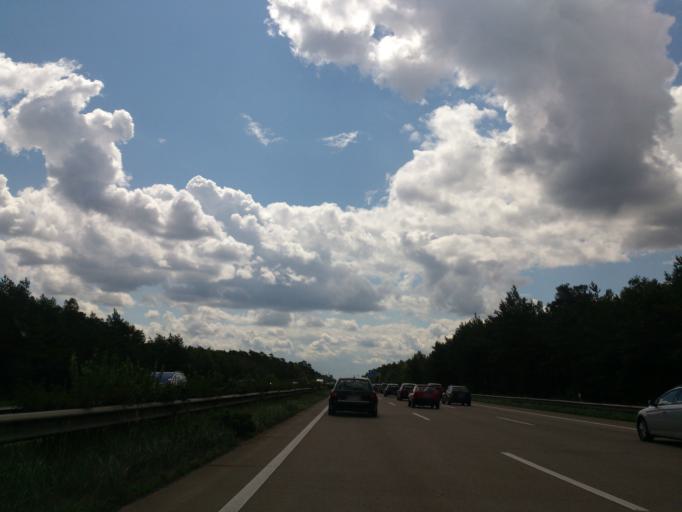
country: DE
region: Lower Saxony
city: Lindwedel
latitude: 52.6239
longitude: 9.7269
